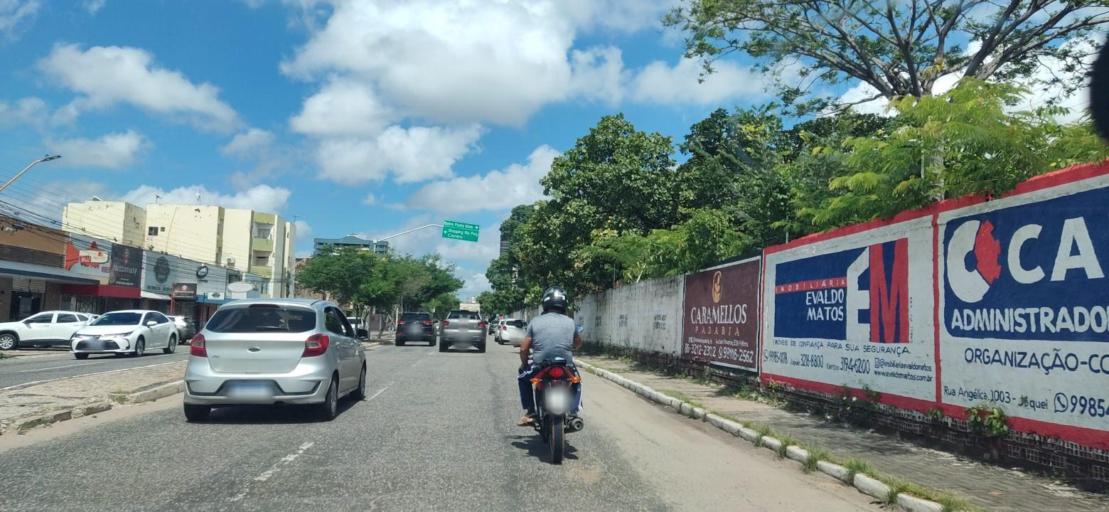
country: BR
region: Piaui
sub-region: Teresina
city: Teresina
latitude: -5.0707
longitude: -42.7698
